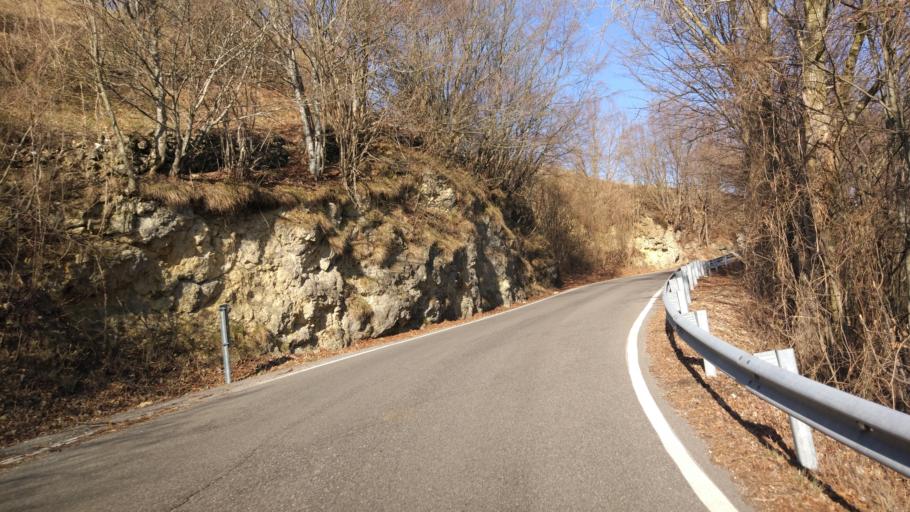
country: IT
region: Veneto
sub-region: Provincia di Verona
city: Selva di Progno
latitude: 45.6171
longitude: 11.1735
